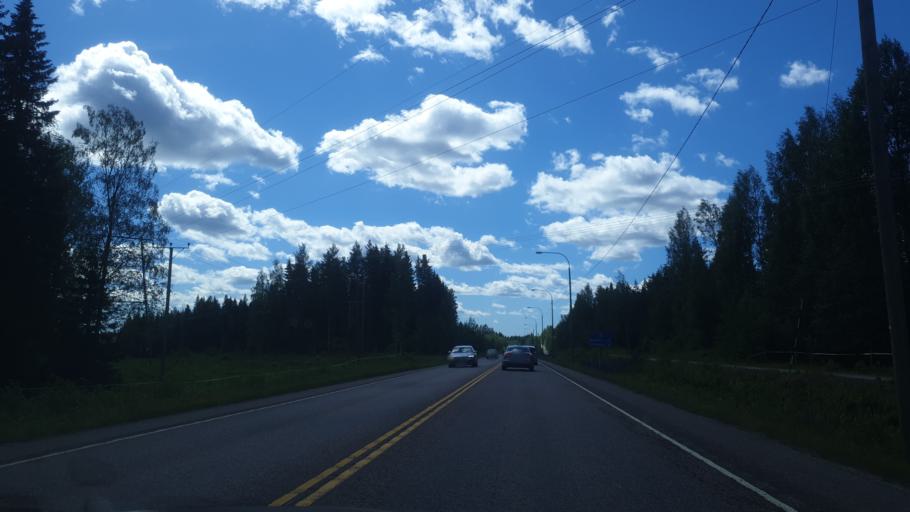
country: FI
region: Northern Savo
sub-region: Varkaus
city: Varkaus
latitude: 62.3980
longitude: 27.8215
